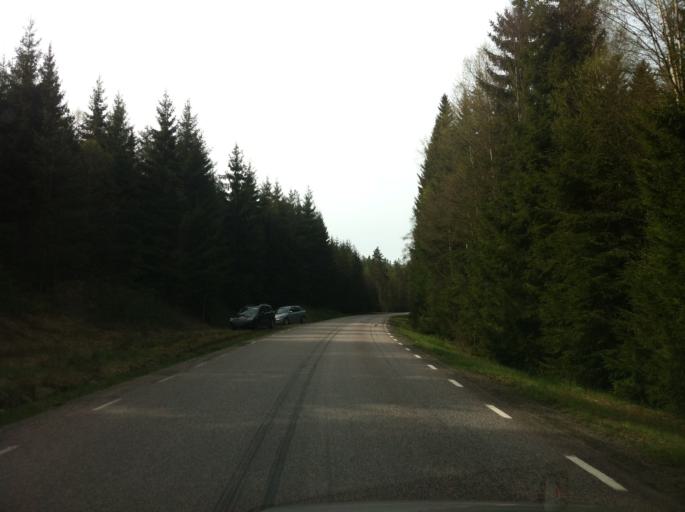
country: SE
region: Vaestra Goetaland
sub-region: Bollebygds Kommun
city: Bollebygd
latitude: 57.5976
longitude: 12.5879
